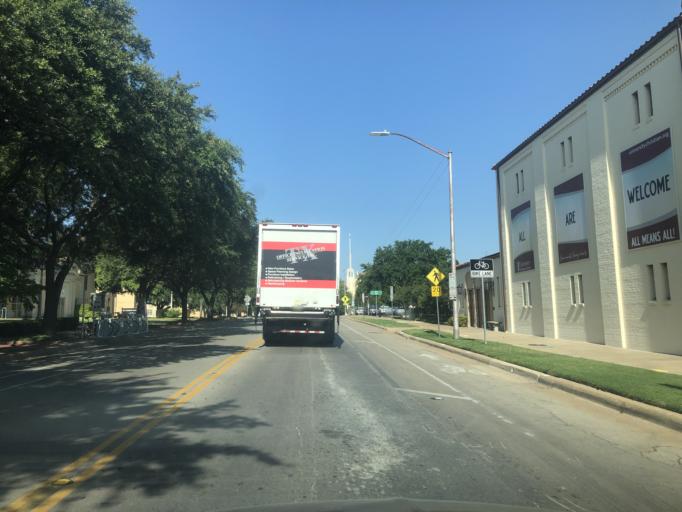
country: US
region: Texas
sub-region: Tarrant County
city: Fort Worth
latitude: 32.7117
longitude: -97.3608
